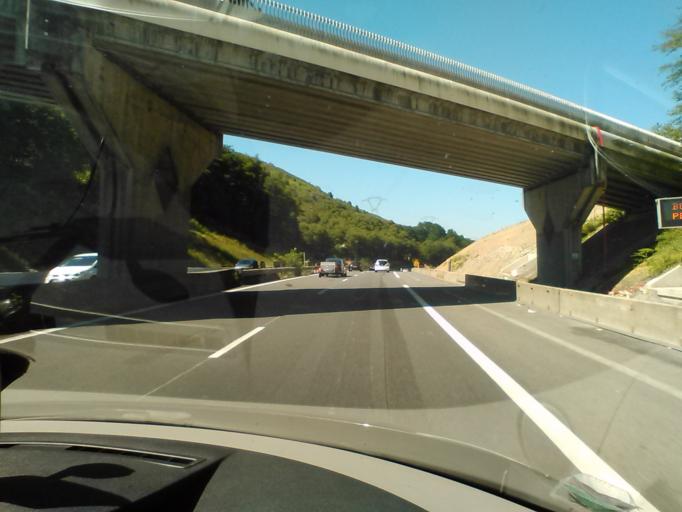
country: FR
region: Aquitaine
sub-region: Departement des Pyrenees-Atlantiques
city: Urrugne
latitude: 43.3419
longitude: -1.7280
